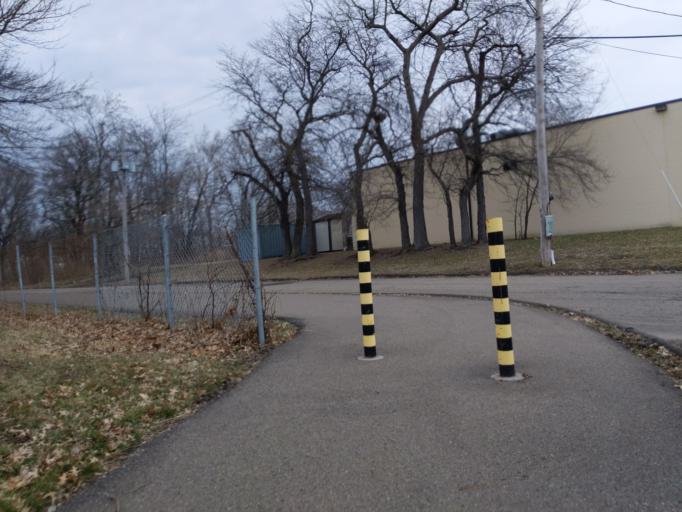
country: US
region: New York
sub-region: Chemung County
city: Elmira
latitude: 42.1066
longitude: -76.8113
